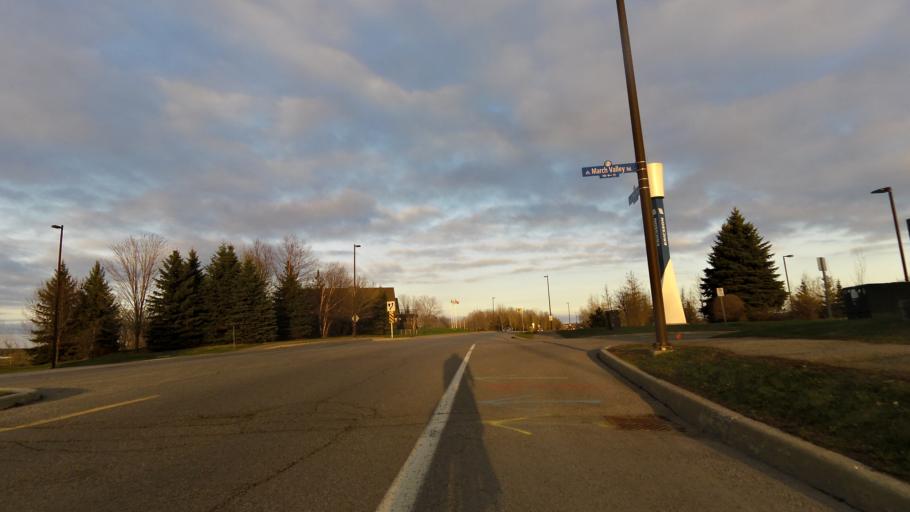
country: CA
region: Ontario
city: Bells Corners
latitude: 45.3525
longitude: -75.9138
